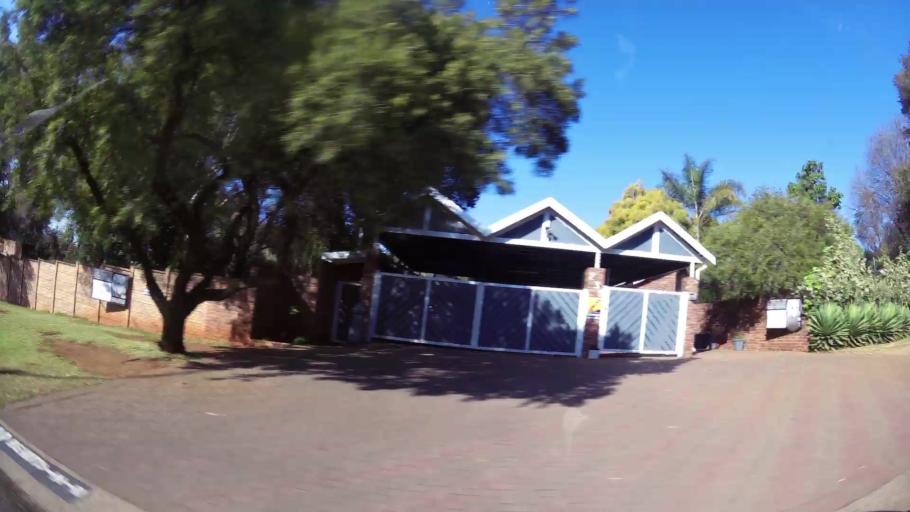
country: ZA
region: Gauteng
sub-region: City of Tshwane Metropolitan Municipality
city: Centurion
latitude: -25.8492
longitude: 28.1703
